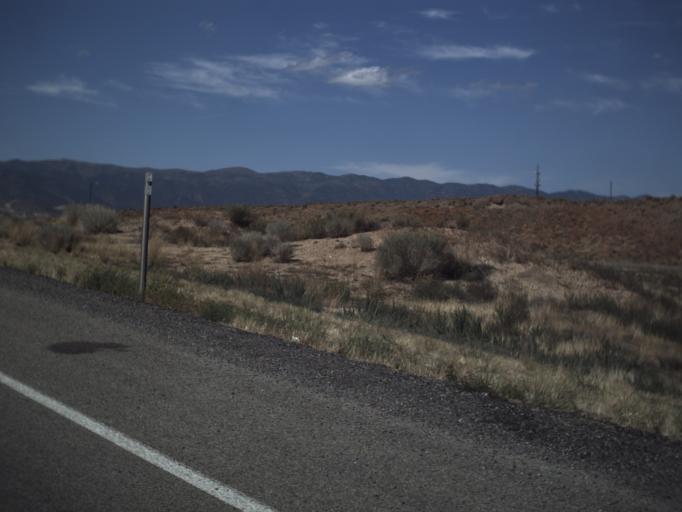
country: US
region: Utah
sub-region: Sevier County
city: Salina
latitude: 38.9343
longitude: -111.8559
